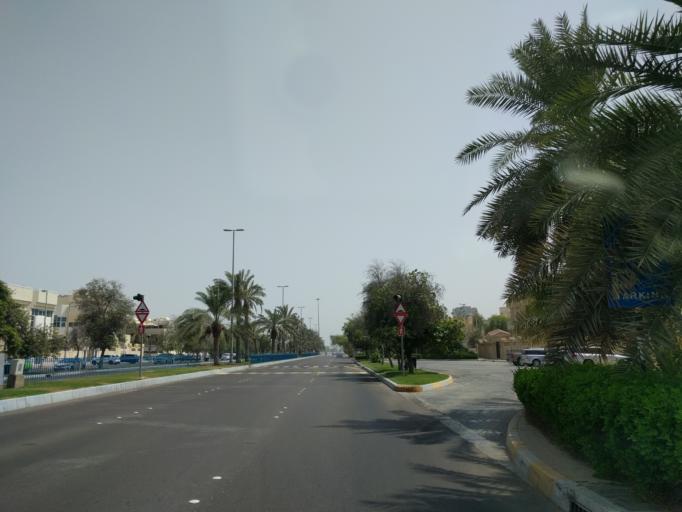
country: AE
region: Abu Dhabi
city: Abu Dhabi
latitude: 24.4423
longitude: 54.4182
